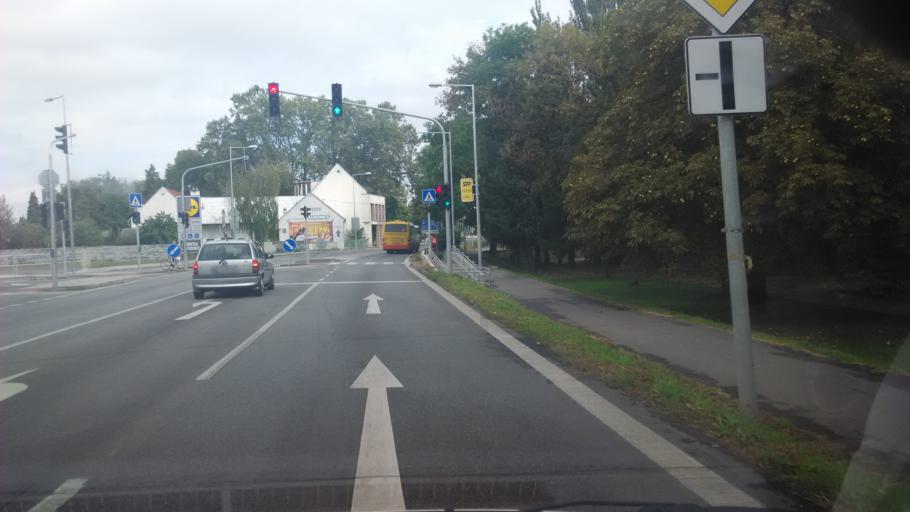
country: SK
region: Trnavsky
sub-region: Okres Trnava
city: Piestany
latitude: 48.5864
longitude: 17.8161
